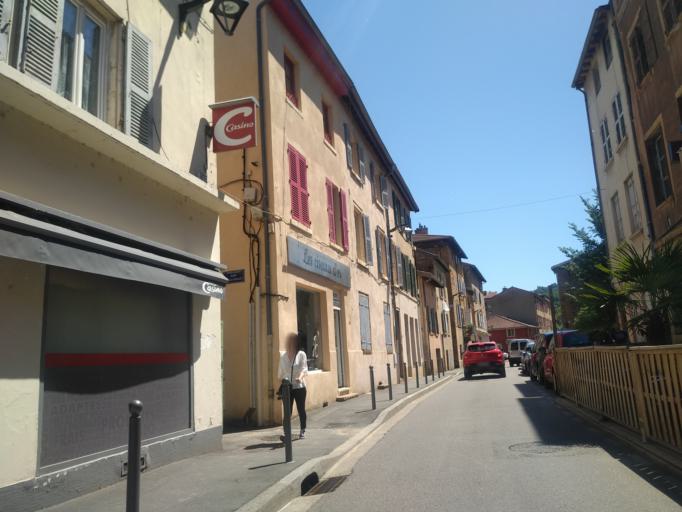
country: FR
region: Rhone-Alpes
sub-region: Departement du Rhone
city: Rochetaillee-sur-Saone
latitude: 45.8452
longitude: 4.8315
